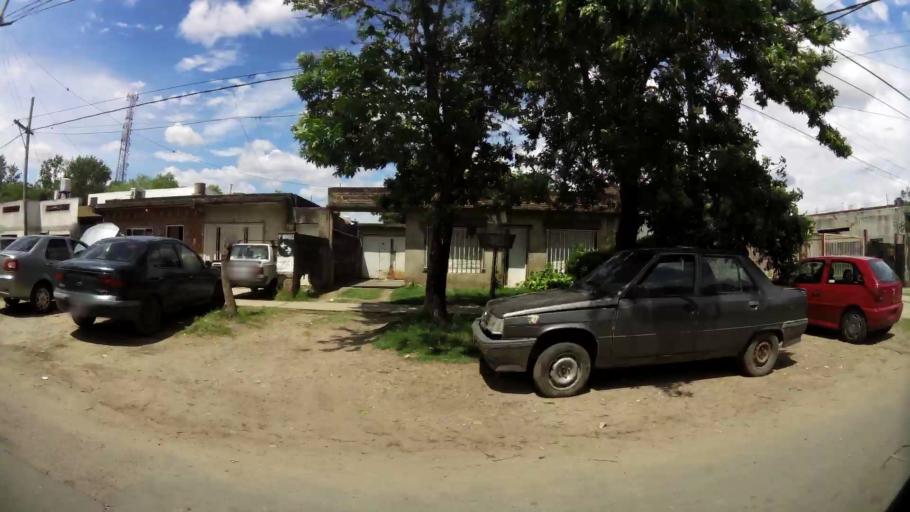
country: AR
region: Santa Fe
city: Gobernador Galvez
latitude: -33.0113
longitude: -60.6421
